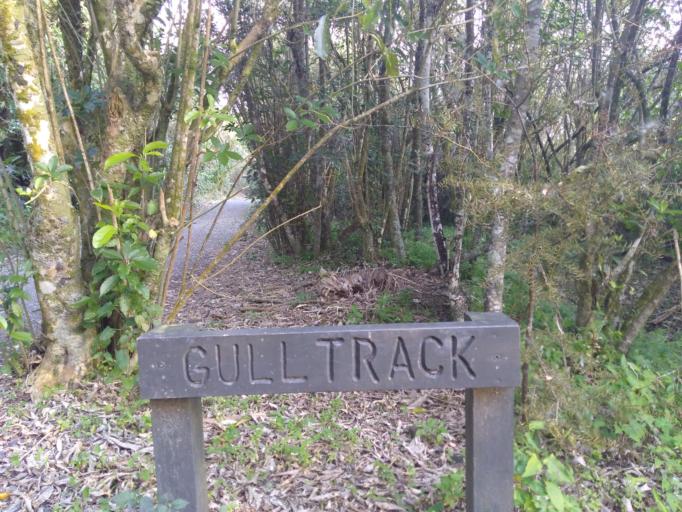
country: NZ
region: Northland
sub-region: Whangarei
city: Whangarei
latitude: -35.7491
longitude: 174.3526
